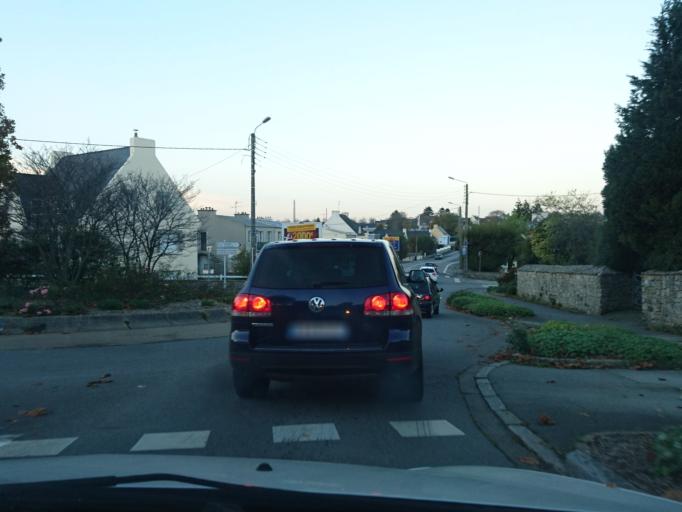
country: FR
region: Brittany
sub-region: Departement du Finistere
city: Brest
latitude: 48.4185
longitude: -4.4872
